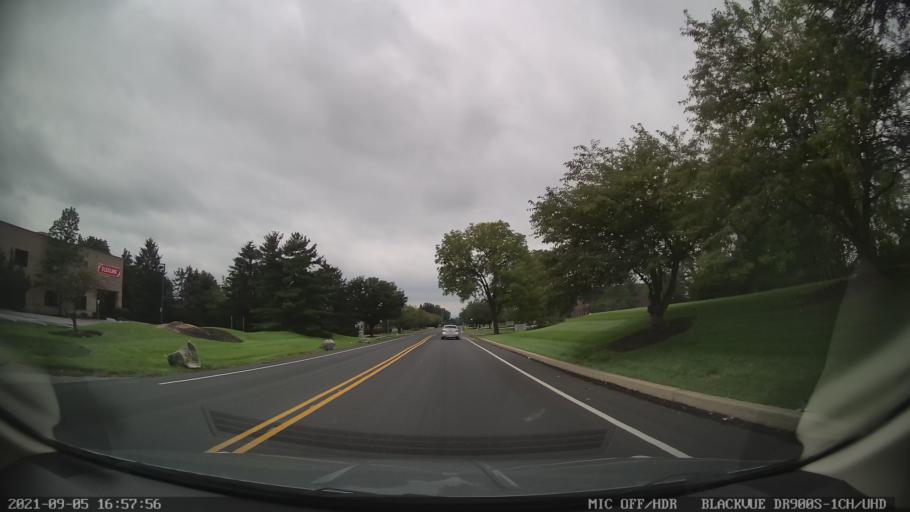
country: US
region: Pennsylvania
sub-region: Lehigh County
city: Trexlertown
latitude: 40.5949
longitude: -75.6078
